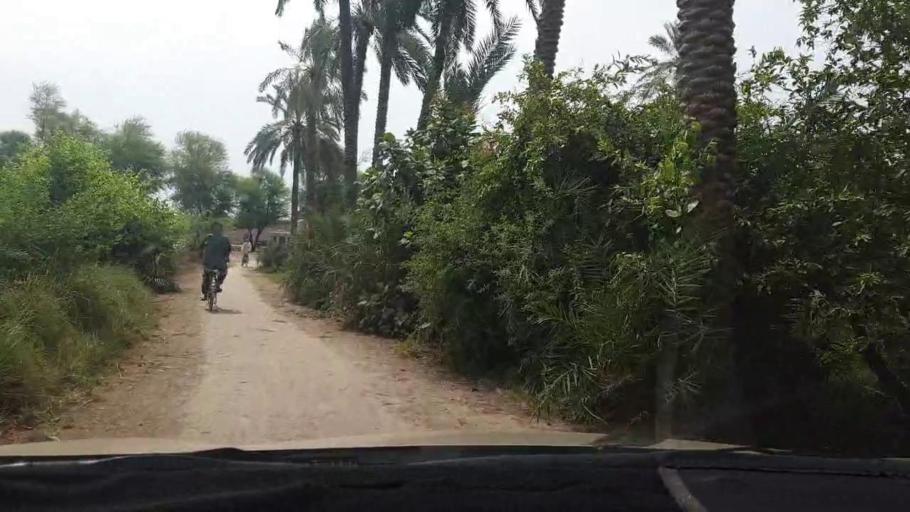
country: PK
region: Sindh
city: Naudero
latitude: 27.6282
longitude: 68.3106
